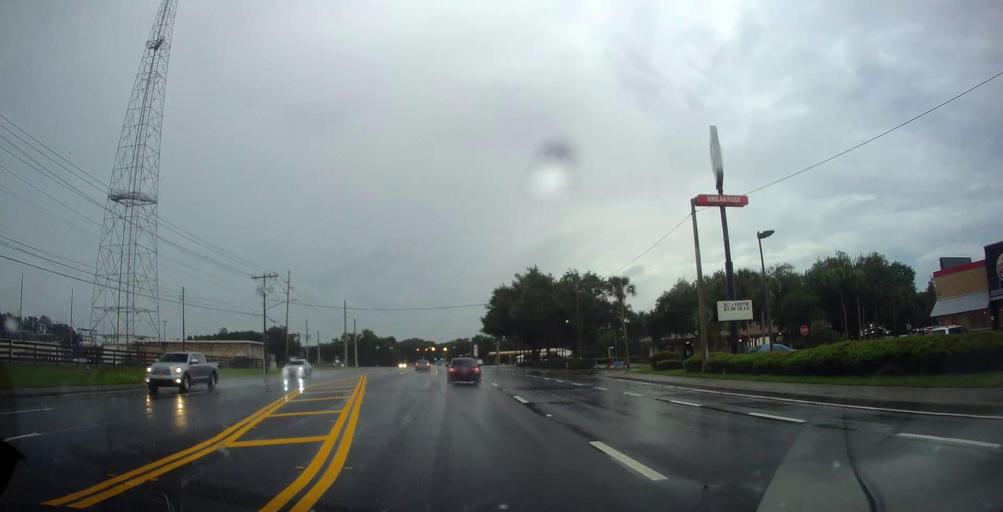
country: US
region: Florida
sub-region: Marion County
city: Ocala
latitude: 29.1596
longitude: -82.0870
